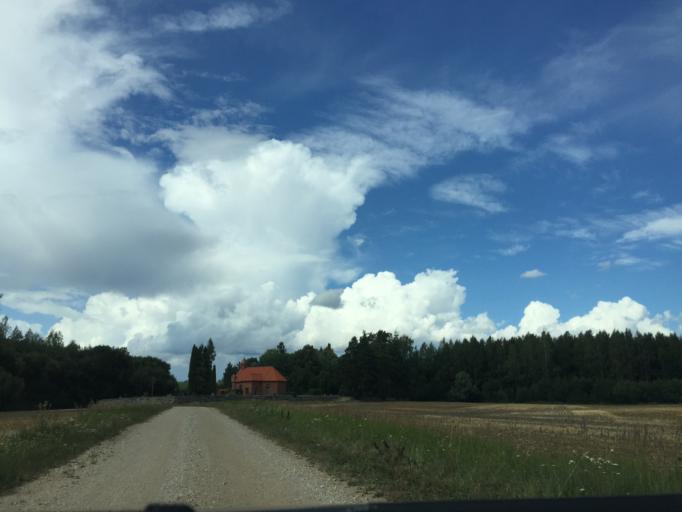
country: LT
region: Siauliu apskritis
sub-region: Joniskis
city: Joniskis
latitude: 56.3572
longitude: 23.6300
